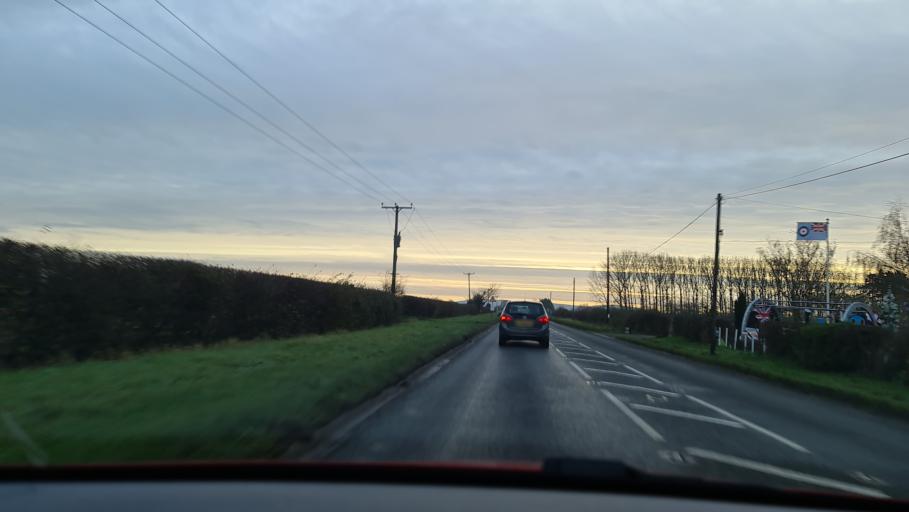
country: GB
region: England
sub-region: Buckinghamshire
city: Haddenham
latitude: 51.7545
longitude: -0.9185
